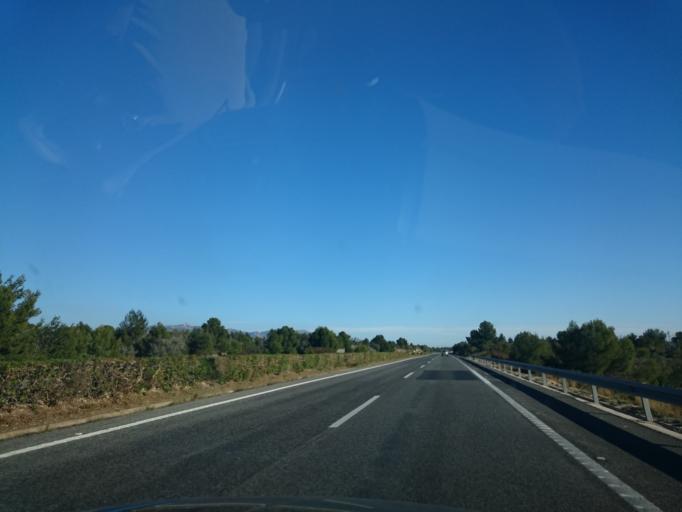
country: ES
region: Catalonia
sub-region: Provincia de Tarragona
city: l'Ametlla de Mar
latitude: 40.8673
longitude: 0.7782
